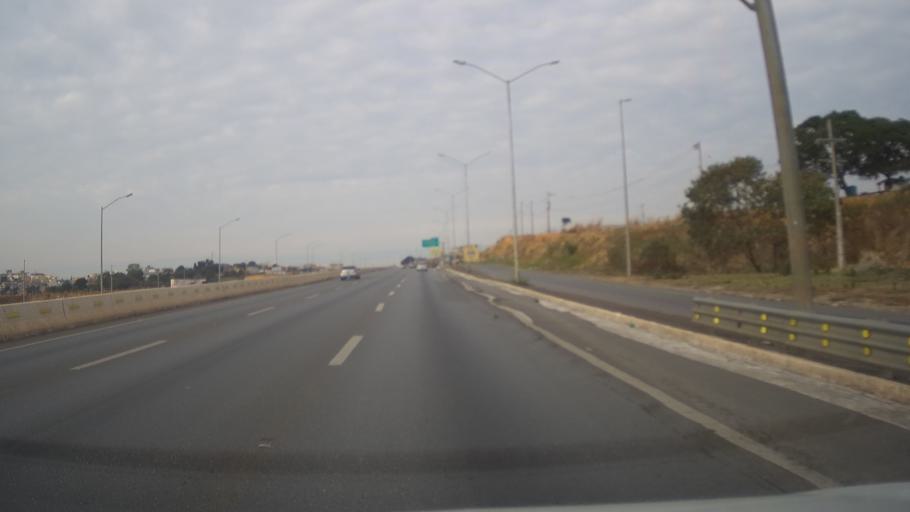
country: BR
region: Minas Gerais
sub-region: Vespasiano
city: Vespasiano
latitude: -19.7392
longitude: -43.9481
